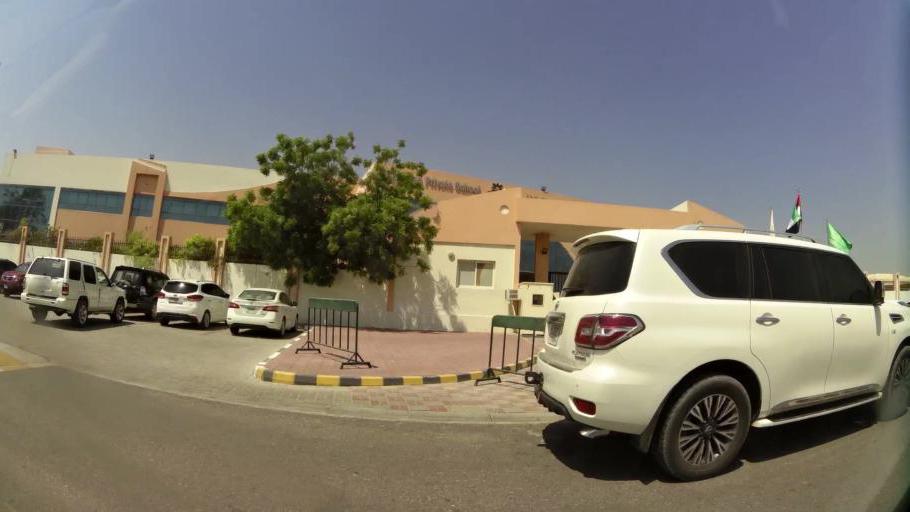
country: AE
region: Ajman
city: Ajman
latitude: 25.4215
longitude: 55.5172
